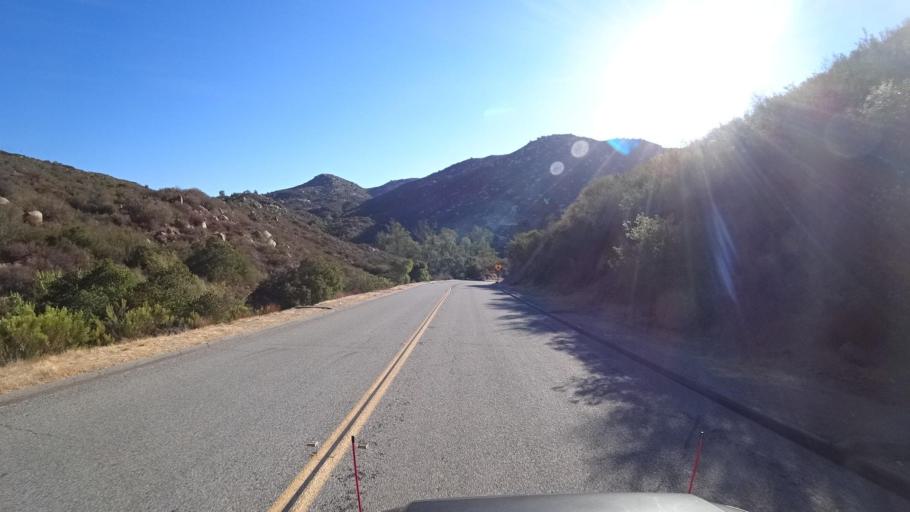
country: US
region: California
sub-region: San Diego County
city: Lakeside
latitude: 32.9006
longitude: -116.8905
